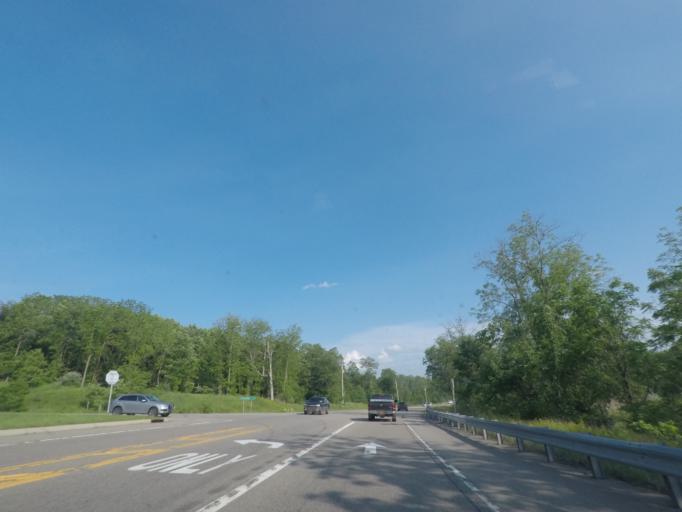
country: US
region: New York
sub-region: Orange County
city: Orange Lake
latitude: 41.4960
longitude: -74.1333
